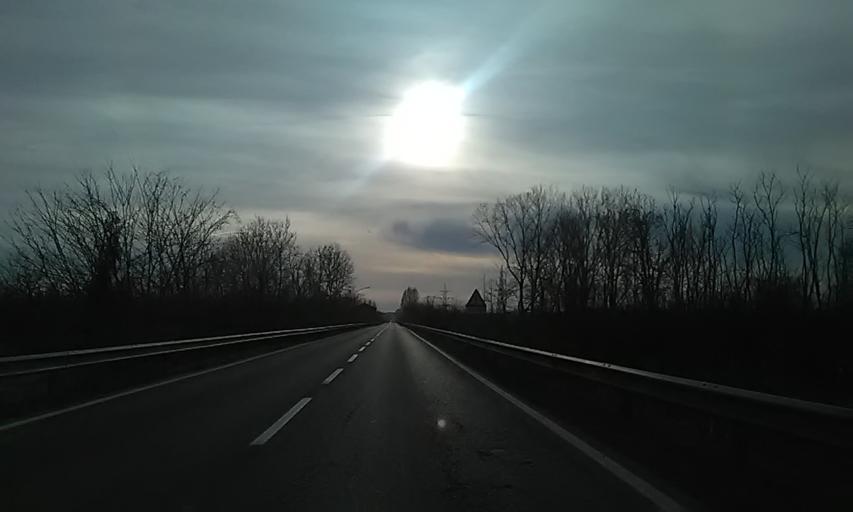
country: IT
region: Piedmont
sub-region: Provincia di Torino
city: Rondissone
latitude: 45.2665
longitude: 7.9773
